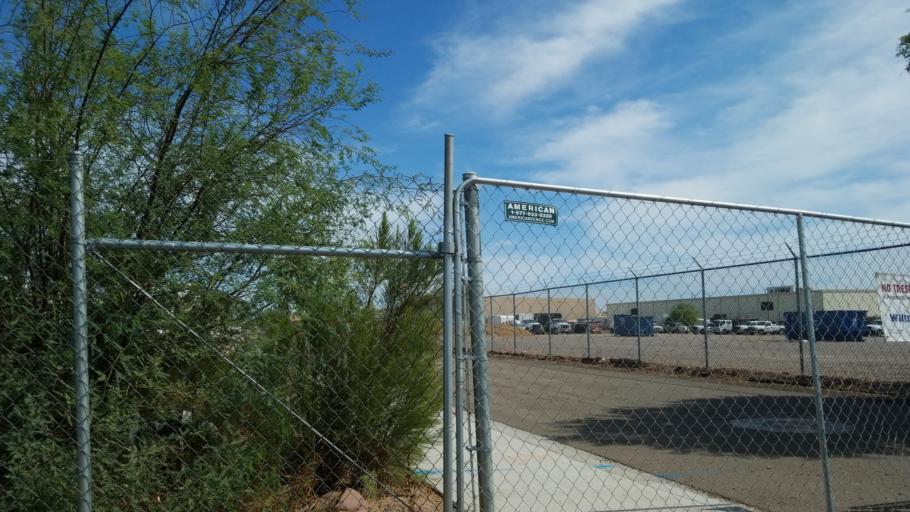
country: US
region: Arizona
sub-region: Maricopa County
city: Tolleson
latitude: 33.4480
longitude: -112.1909
